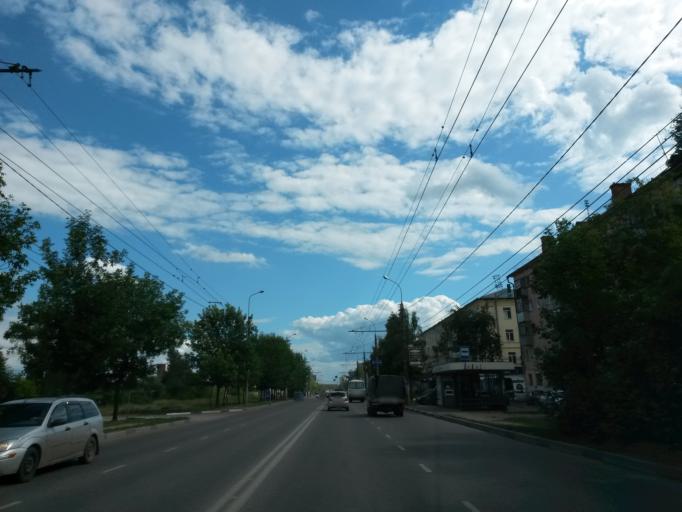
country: RU
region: Ivanovo
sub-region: Gorod Ivanovo
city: Ivanovo
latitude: 56.9723
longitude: 41.0117
